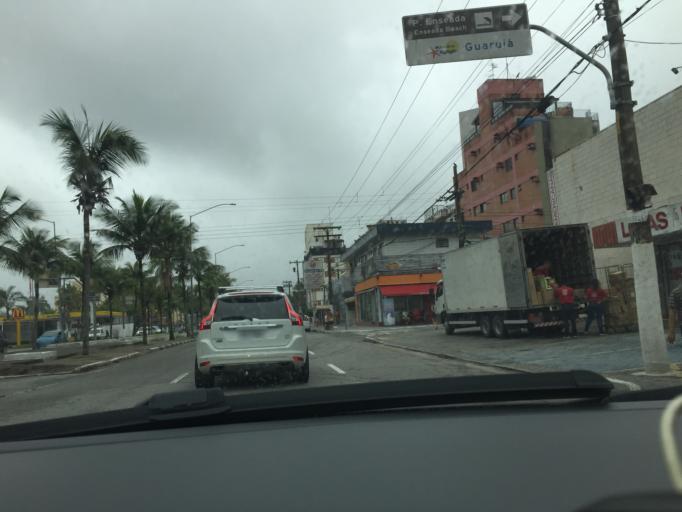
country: BR
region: Sao Paulo
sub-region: Guaruja
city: Guaruja
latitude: -23.9830
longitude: -46.2342
